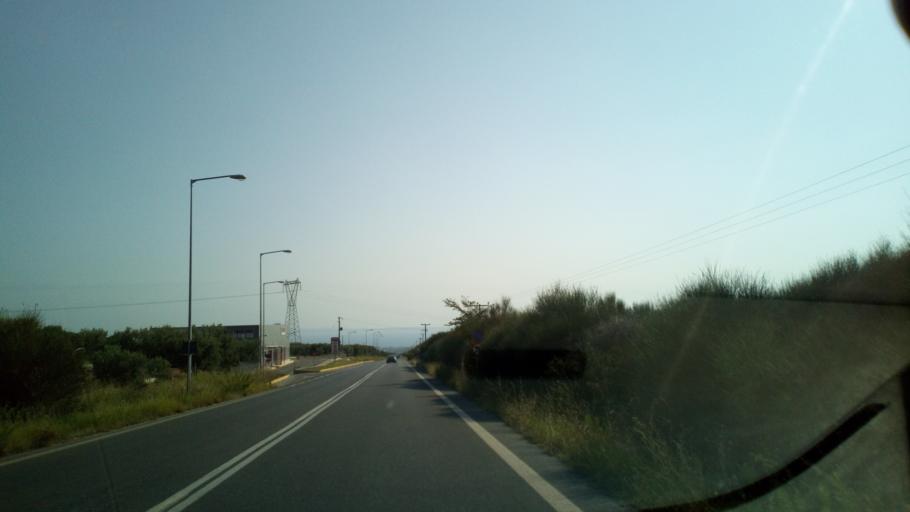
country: GR
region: Central Macedonia
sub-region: Nomos Chalkidikis
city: Kalyves Polygyrou
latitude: 40.3143
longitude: 23.4429
